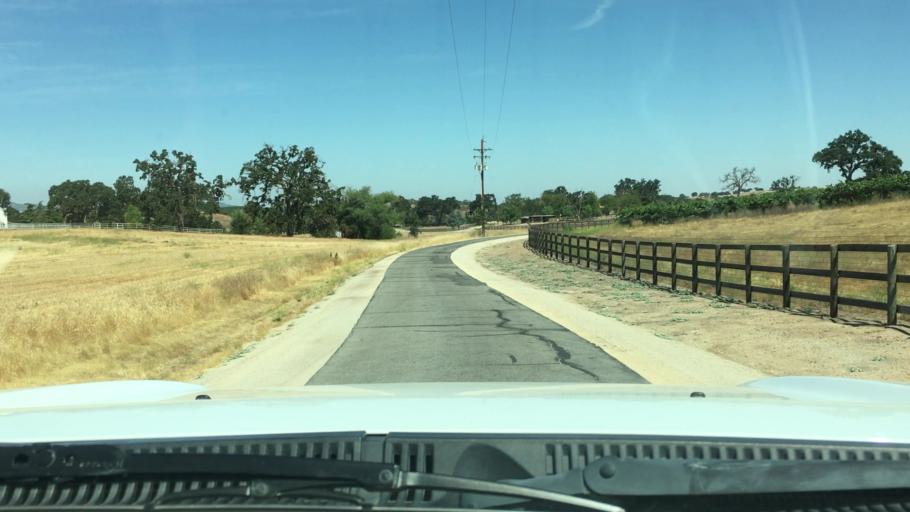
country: US
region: California
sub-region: San Luis Obispo County
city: Paso Robles
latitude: 35.5743
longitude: -120.6023
